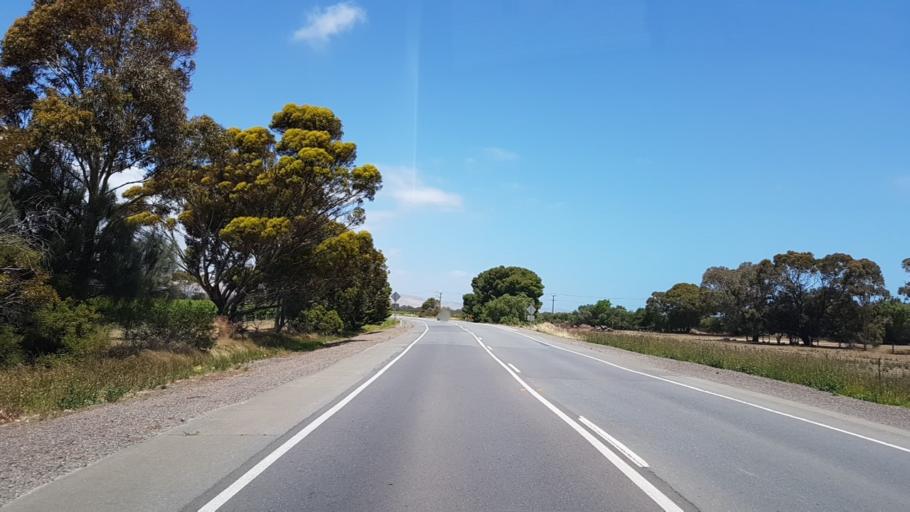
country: AU
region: South Australia
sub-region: Onkaparinga
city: Aldinga
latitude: -35.2844
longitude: 138.4731
